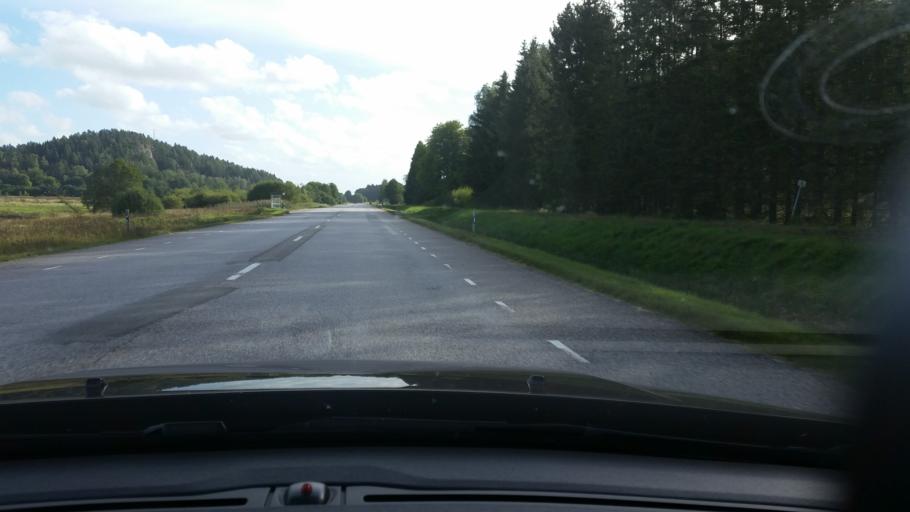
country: SE
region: Vaestra Goetaland
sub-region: Lilla Edets Kommun
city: Lodose
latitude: 58.0751
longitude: 12.1534
